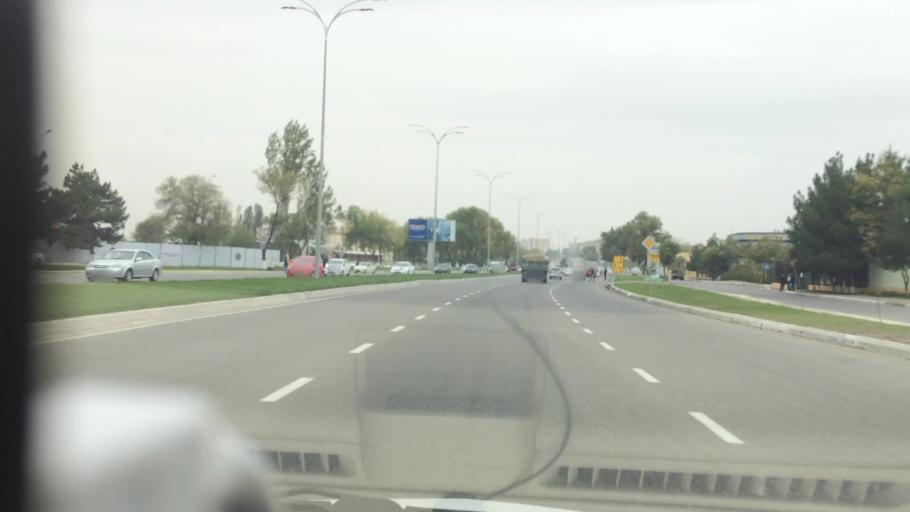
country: UZ
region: Toshkent
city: Salor
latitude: 41.3009
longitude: 69.3457
